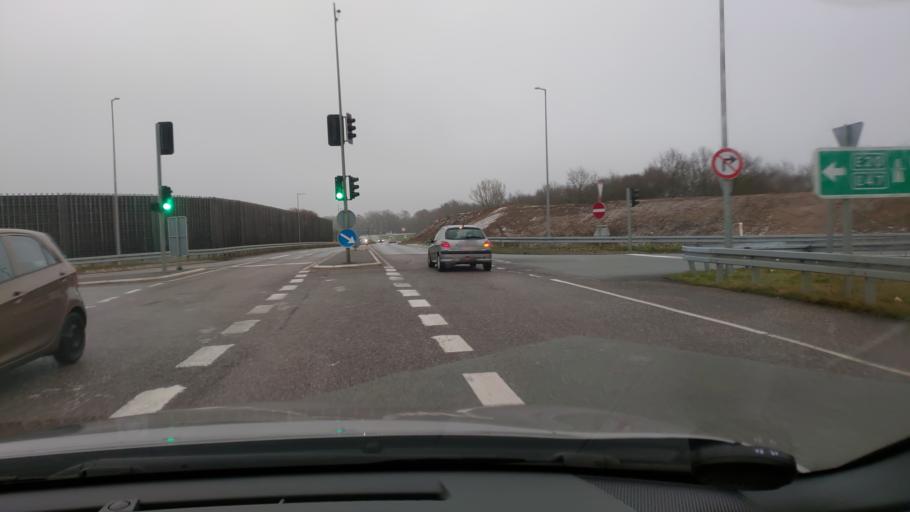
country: DK
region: Zealand
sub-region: Solrod Kommune
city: Solrod Strand
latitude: 55.5454
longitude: 12.2182
